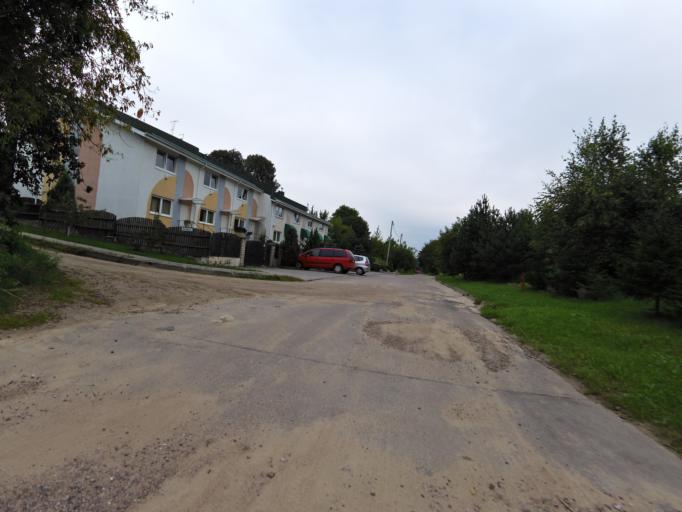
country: LT
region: Vilnius County
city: Rasos
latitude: 54.6603
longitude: 25.2910
